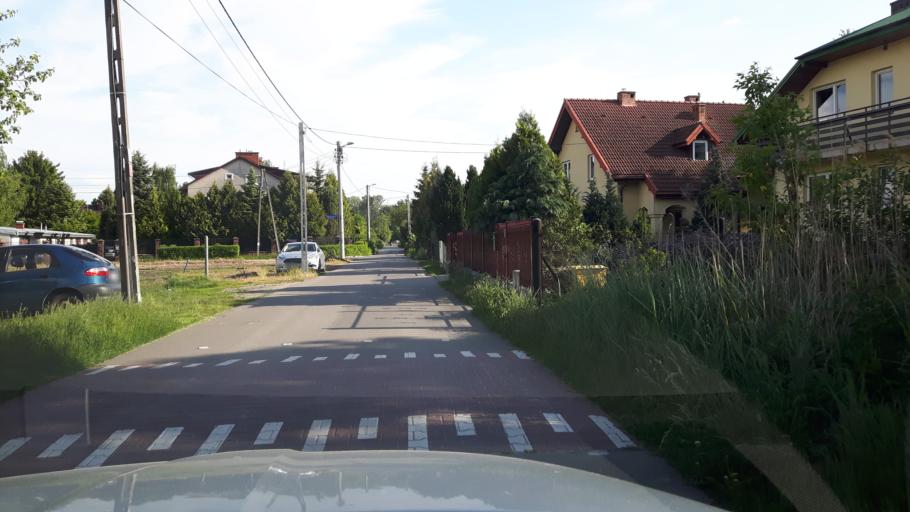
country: PL
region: Masovian Voivodeship
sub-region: Warszawa
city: Praga Poludnie
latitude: 52.2559
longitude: 21.1208
